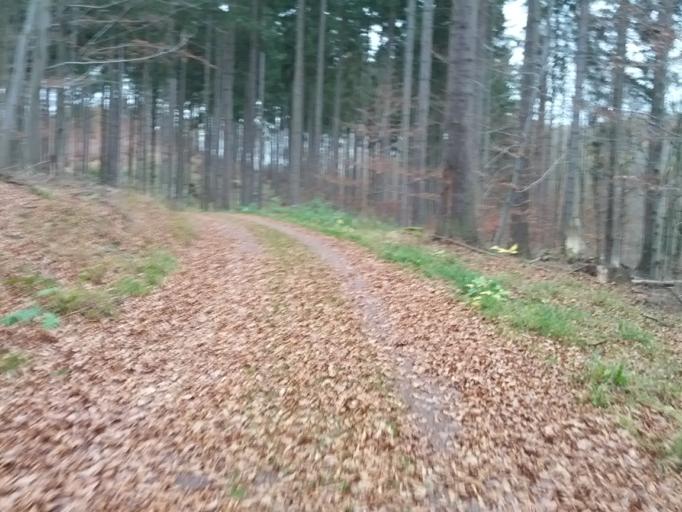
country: DE
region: Thuringia
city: Eisenach
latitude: 50.9412
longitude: 10.3116
